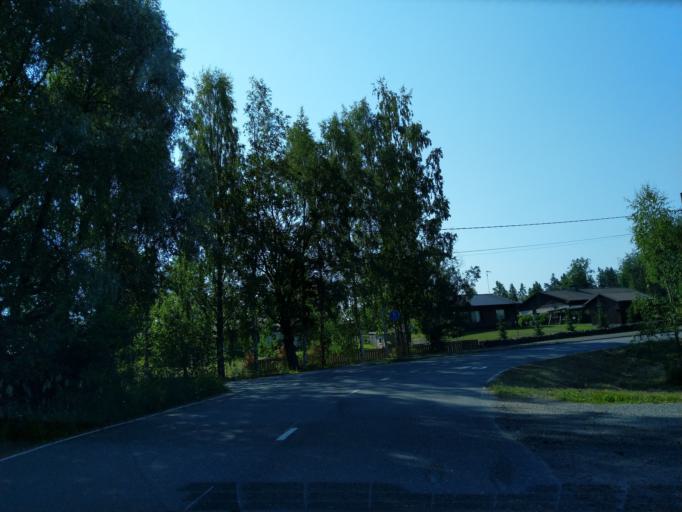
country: FI
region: Satakunta
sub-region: Pori
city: Pomarkku
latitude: 61.7069
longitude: 22.0282
